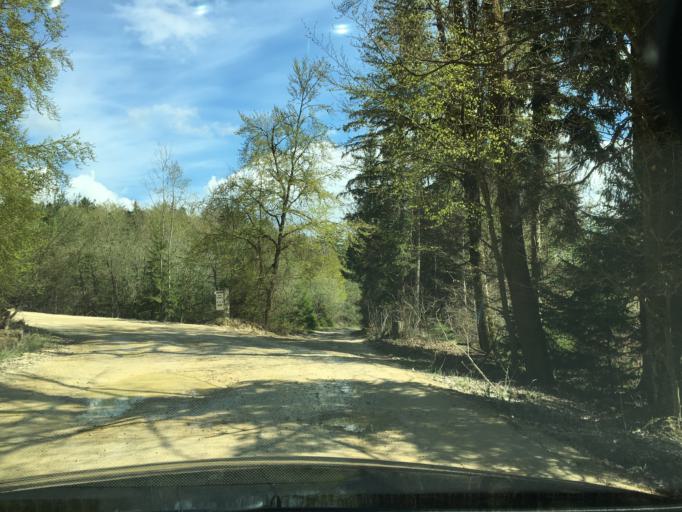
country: DE
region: Bavaria
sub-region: Regierungsbezirk Mittelfranken
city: Solnhofen
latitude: 48.8879
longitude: 10.9653
